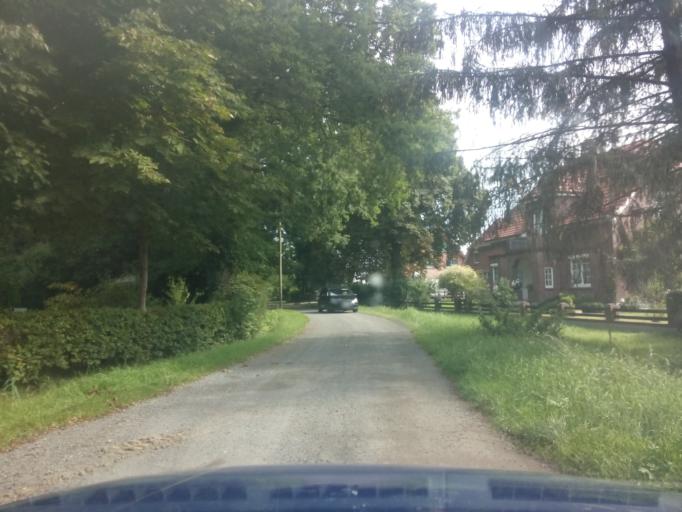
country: DE
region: Lower Saxony
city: Osterholz-Scharmbeck
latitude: 53.2381
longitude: 8.7640
